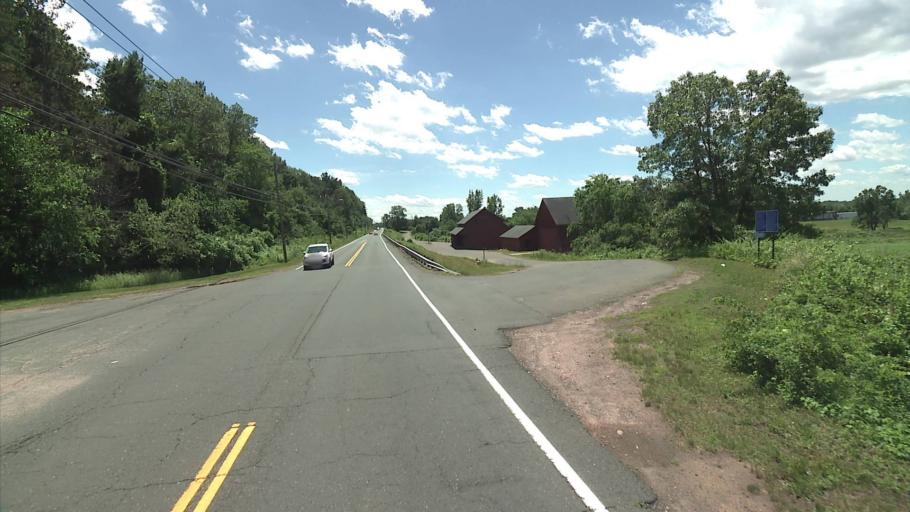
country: US
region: Massachusetts
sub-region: Hampden County
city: East Longmeadow
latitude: 42.0231
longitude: -72.5149
